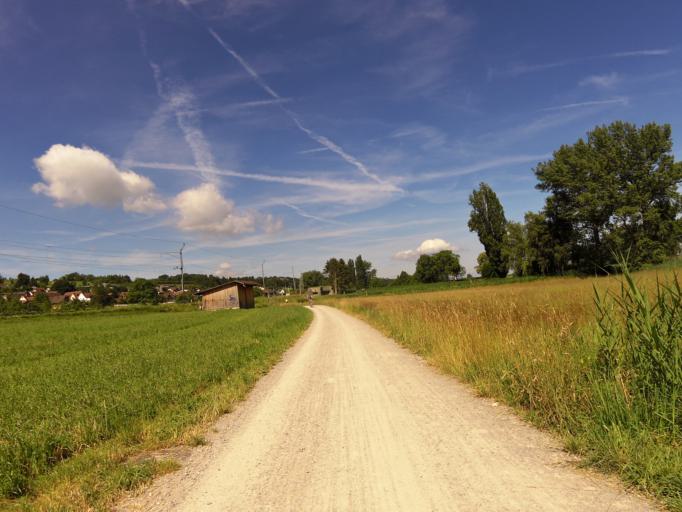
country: CH
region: Thurgau
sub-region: Kreuzlingen District
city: Tagerwilen
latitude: 47.6634
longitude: 9.1142
